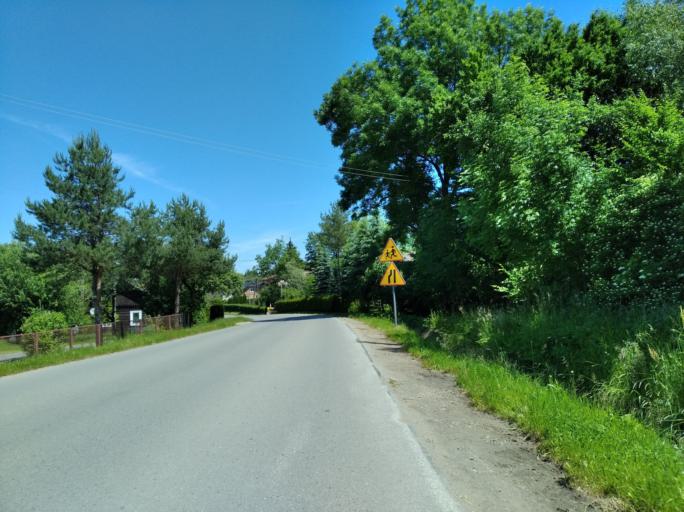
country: PL
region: Subcarpathian Voivodeship
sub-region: Powiat jasielski
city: Tarnowiec
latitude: 49.6936
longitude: 21.5528
